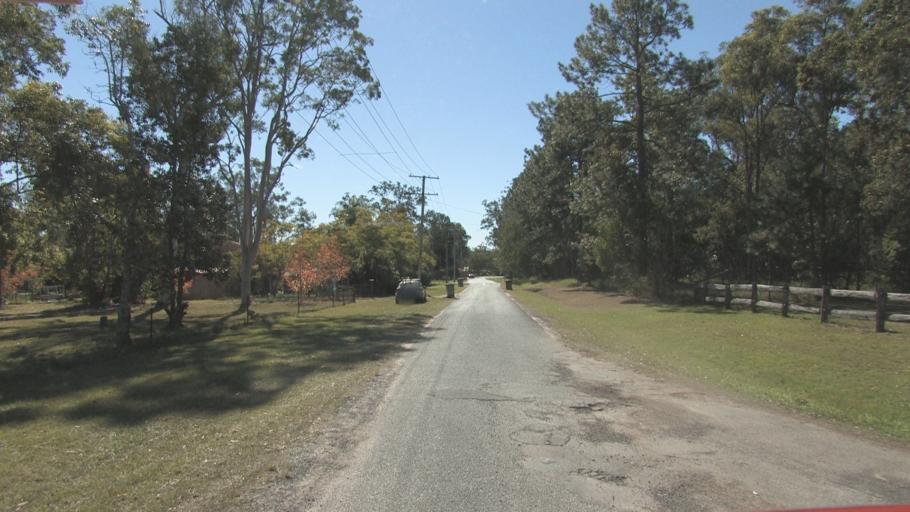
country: AU
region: Queensland
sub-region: Logan
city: Logan Reserve
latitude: -27.7207
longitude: 153.0645
